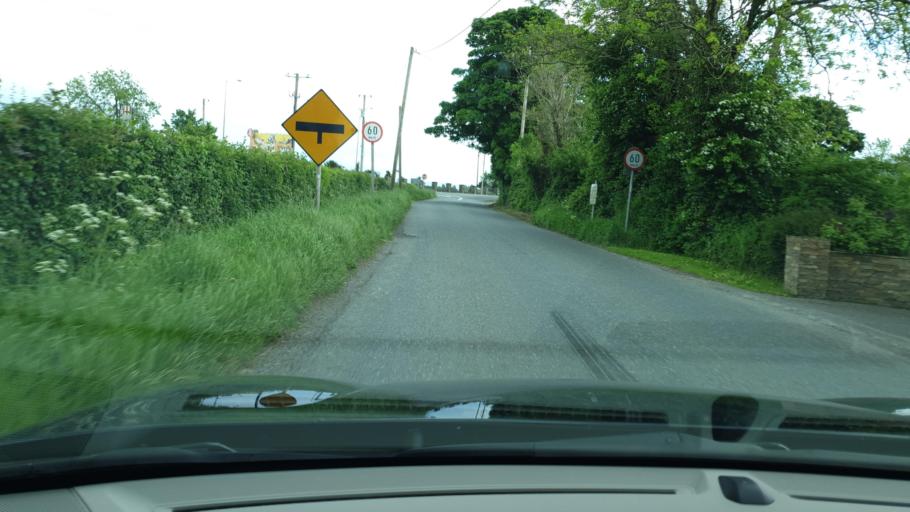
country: IE
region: Leinster
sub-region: An Mhi
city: Ashbourne
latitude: 53.5302
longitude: -6.4207
